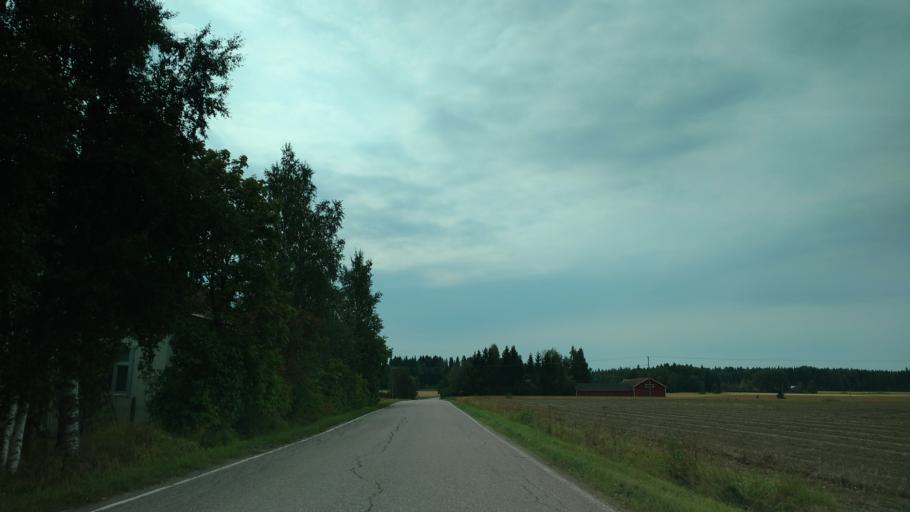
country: FI
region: Haeme
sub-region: Forssa
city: Ypaejae
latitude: 60.7865
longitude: 23.2707
